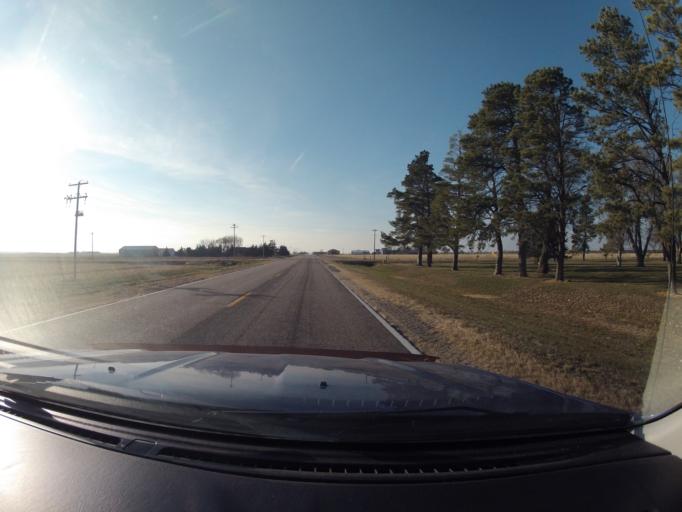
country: US
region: Nebraska
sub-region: Buffalo County
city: Kearney
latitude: 40.6410
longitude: -99.0075
